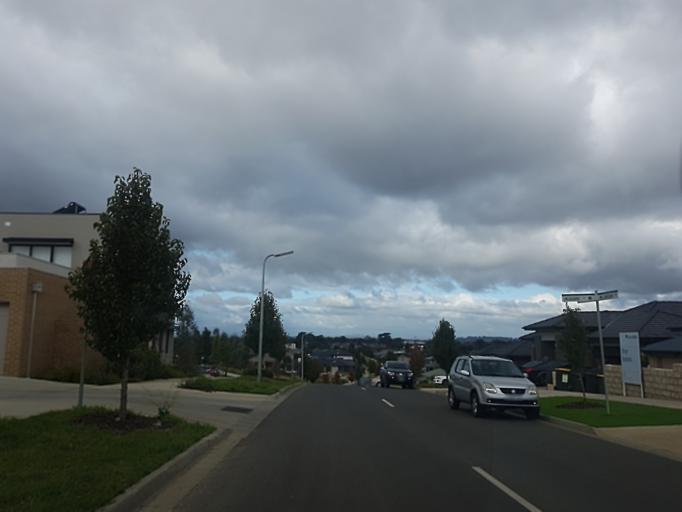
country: AU
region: Victoria
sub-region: Whittlesea
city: Mernda
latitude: -37.5965
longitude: 145.0805
